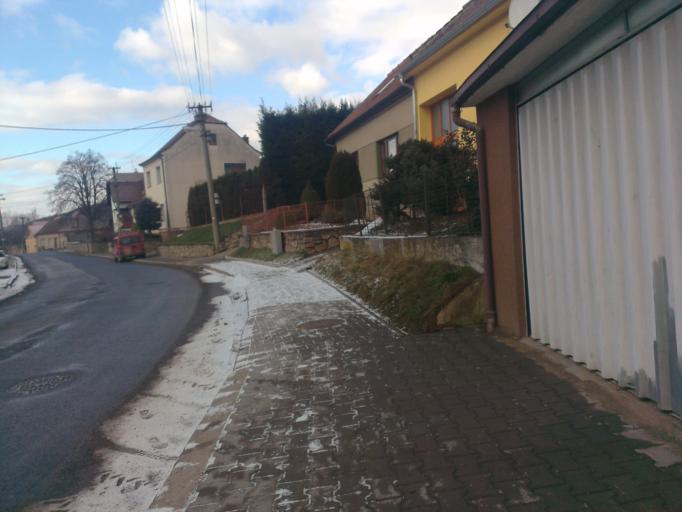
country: CZ
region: South Moravian
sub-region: Okres Brno-Venkov
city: Lelekovice
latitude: 49.2904
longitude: 16.5869
